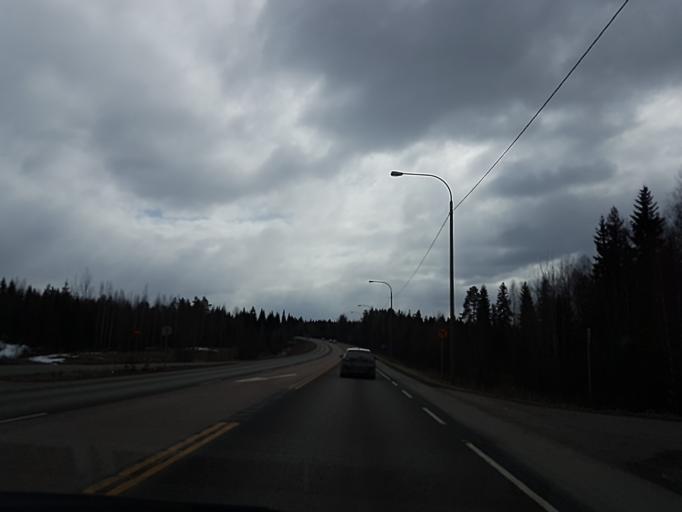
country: FI
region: Northern Savo
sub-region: Varkaus
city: Varkaus
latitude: 62.3645
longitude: 27.8098
